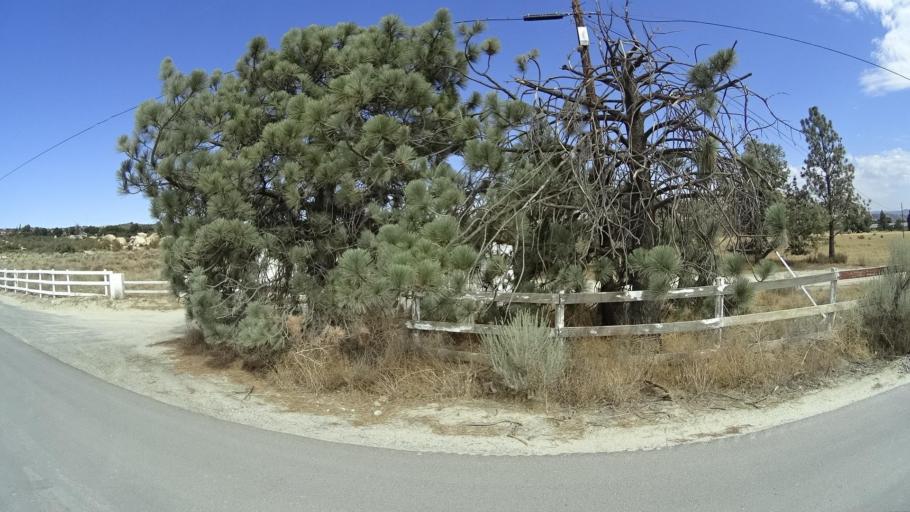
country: MX
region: Baja California
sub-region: Tecate
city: Cereso del Hongo
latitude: 32.6394
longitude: -116.2728
